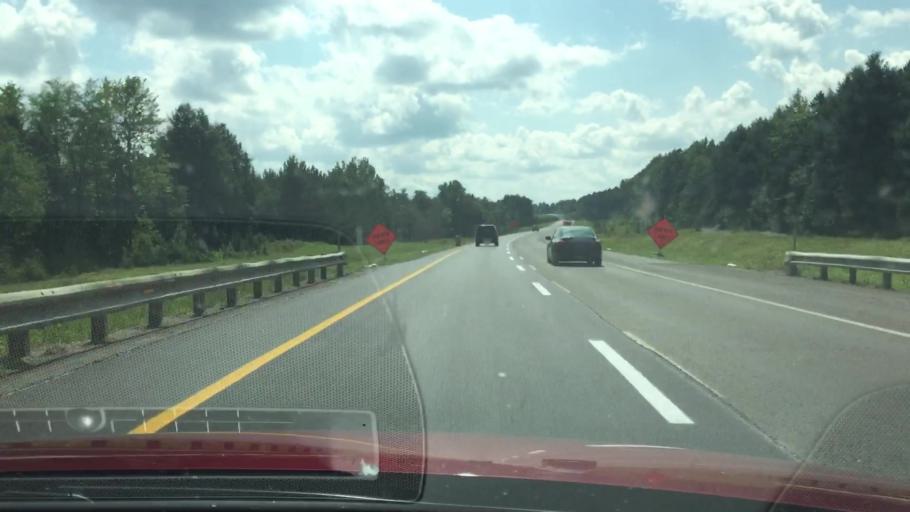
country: US
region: Maine
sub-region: Penobscot County
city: Medway
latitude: 45.6389
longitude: -68.5006
